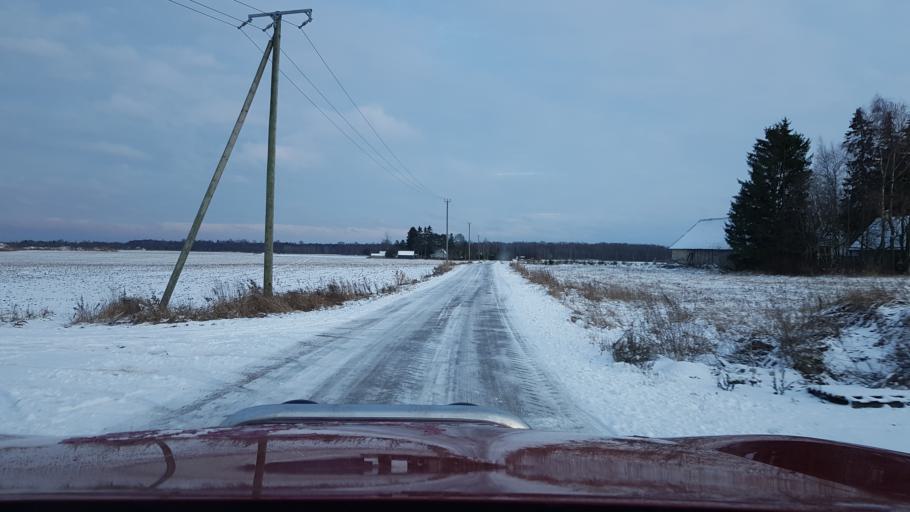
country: EE
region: Harju
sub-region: Maardu linn
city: Maardu
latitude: 59.4296
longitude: 25.0327
